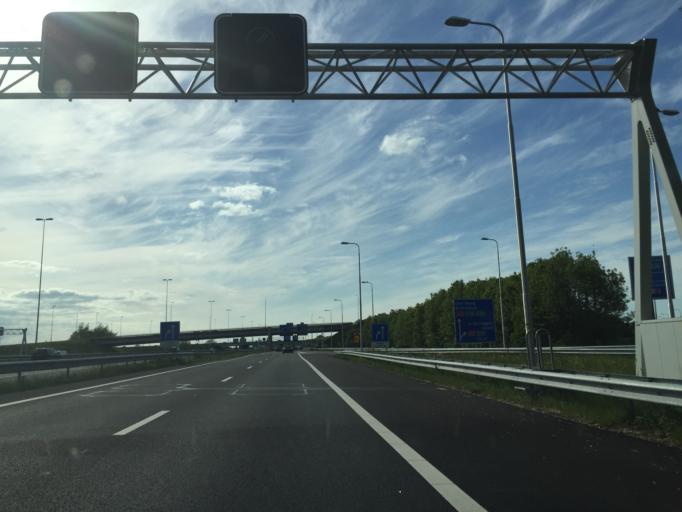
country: NL
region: Utrecht
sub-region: Gemeente Nieuwegein
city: Nieuwegein
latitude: 52.0642
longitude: 5.0767
